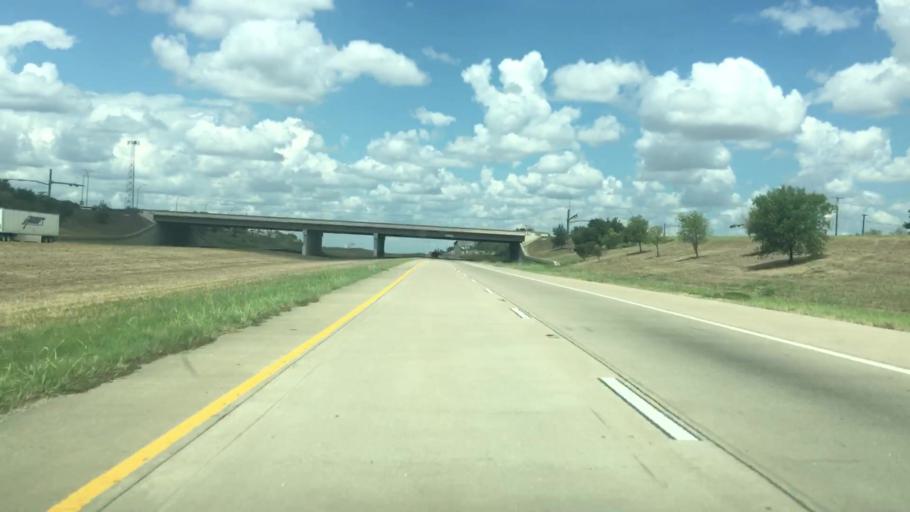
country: US
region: Texas
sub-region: Williamson County
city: Georgetown
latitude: 30.6403
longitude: -97.6293
